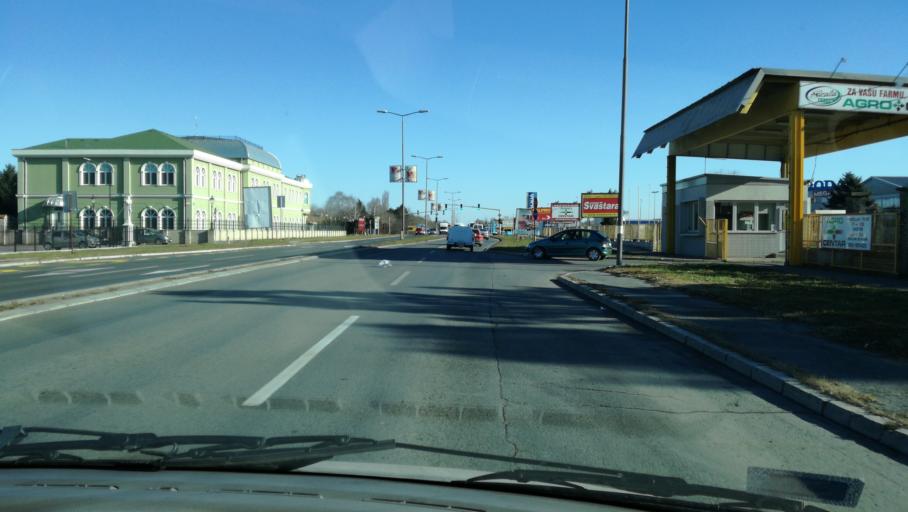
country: RS
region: Autonomna Pokrajina Vojvodina
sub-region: Severnobacki Okrug
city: Subotica
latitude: 46.1019
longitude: 19.6993
